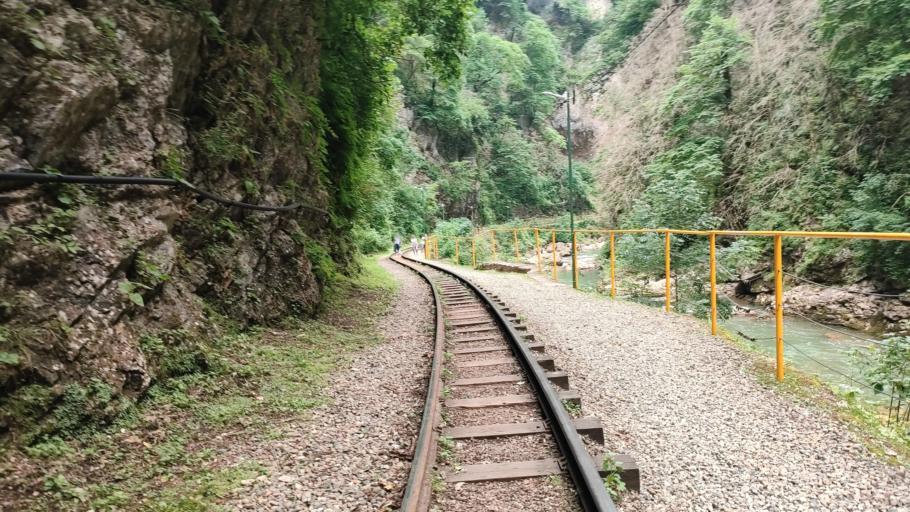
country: RU
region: Krasnodarskiy
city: Neftegorsk
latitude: 44.2192
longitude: 39.9100
